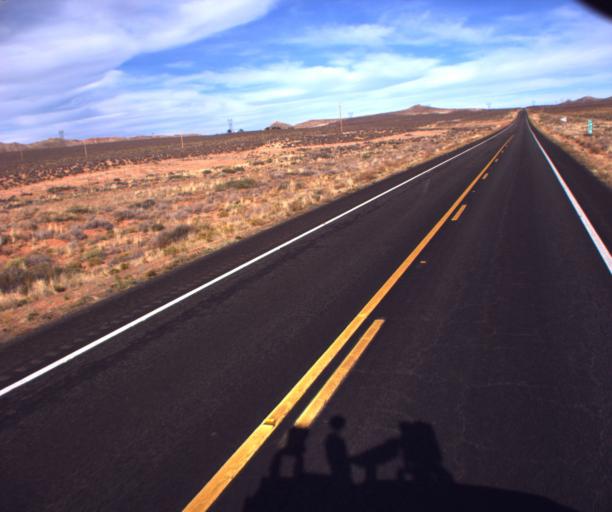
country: US
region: Arizona
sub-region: Apache County
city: Many Farms
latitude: 36.9352
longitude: -109.5613
